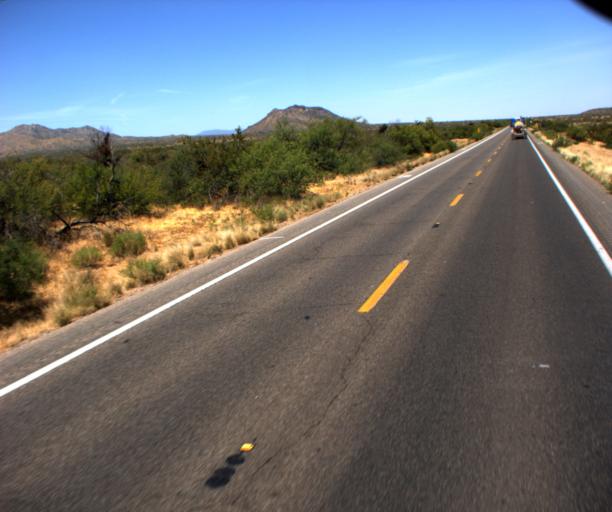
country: US
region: Arizona
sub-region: Gila County
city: Peridot
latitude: 33.3160
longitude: -110.5223
